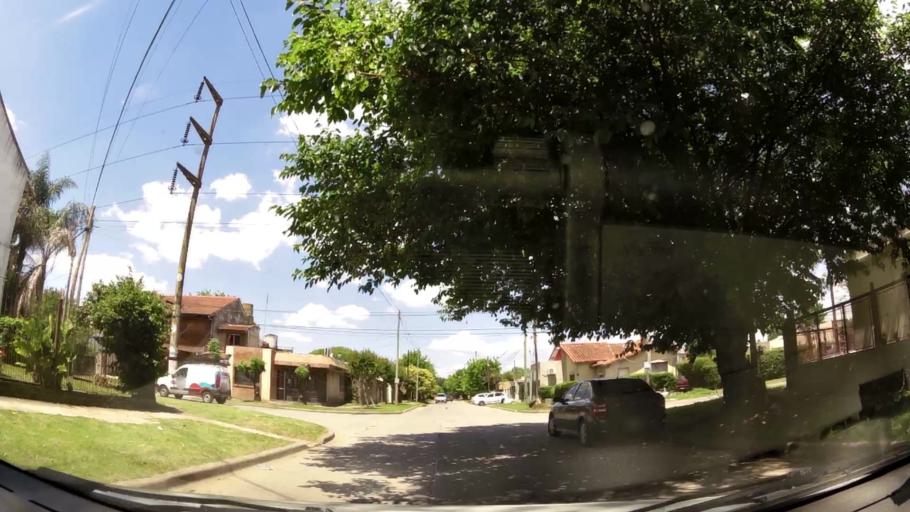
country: AR
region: Buenos Aires
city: Ituzaingo
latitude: -34.6439
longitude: -58.6866
